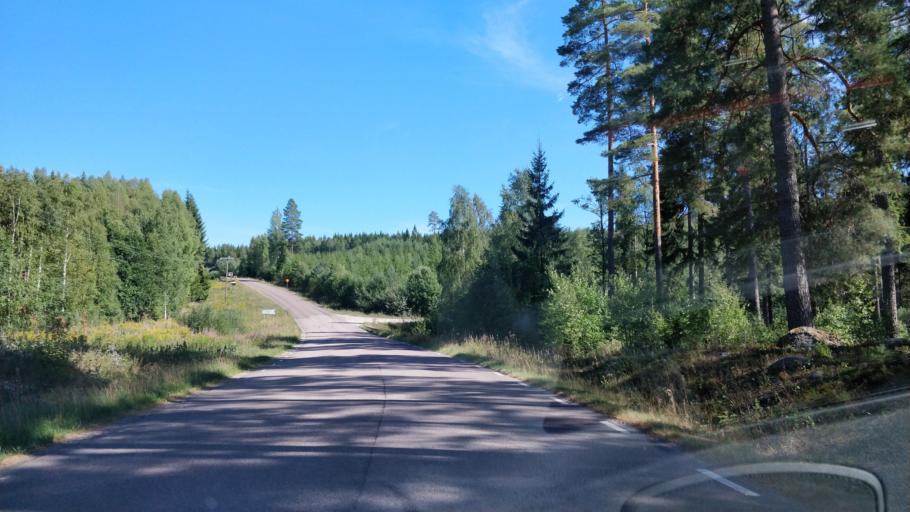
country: SE
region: Vaermland
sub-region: Hagfors Kommun
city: Hagfors
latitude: 60.0388
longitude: 13.7207
